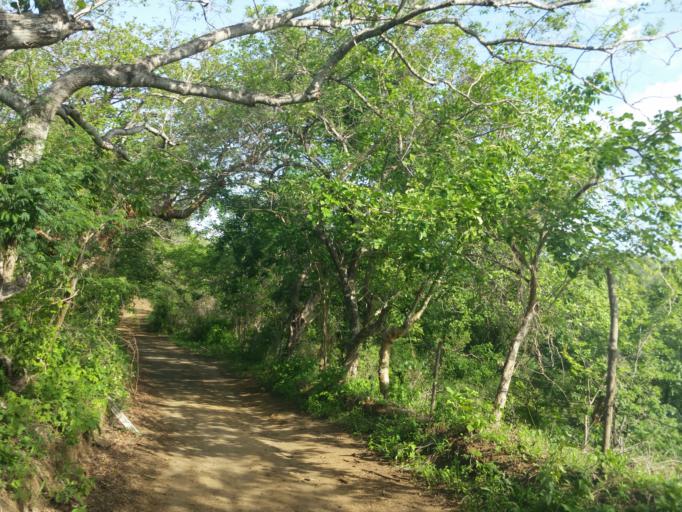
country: NI
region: Managua
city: Managua
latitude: 12.0985
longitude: -86.2832
